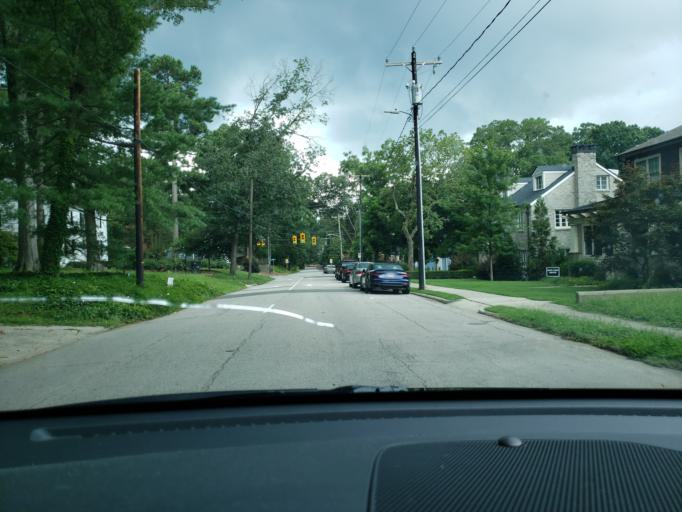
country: US
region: North Carolina
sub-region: Durham County
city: Durham
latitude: 35.9878
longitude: -78.9120
